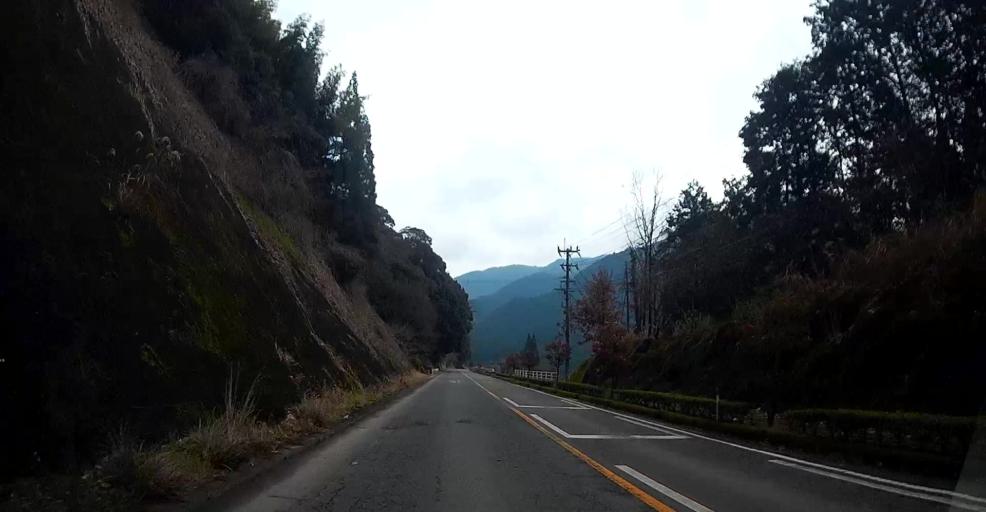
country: JP
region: Kumamoto
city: Matsubase
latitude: 32.6160
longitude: 130.8415
